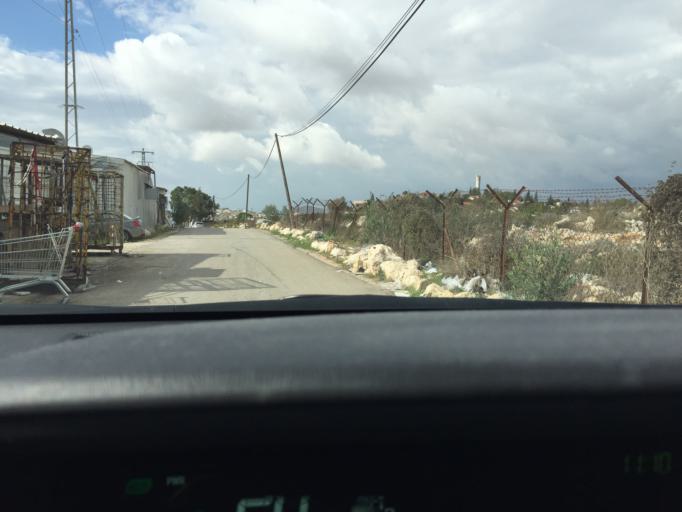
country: PS
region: West Bank
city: Kafr ad Dik
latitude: 32.0698
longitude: 35.0689
